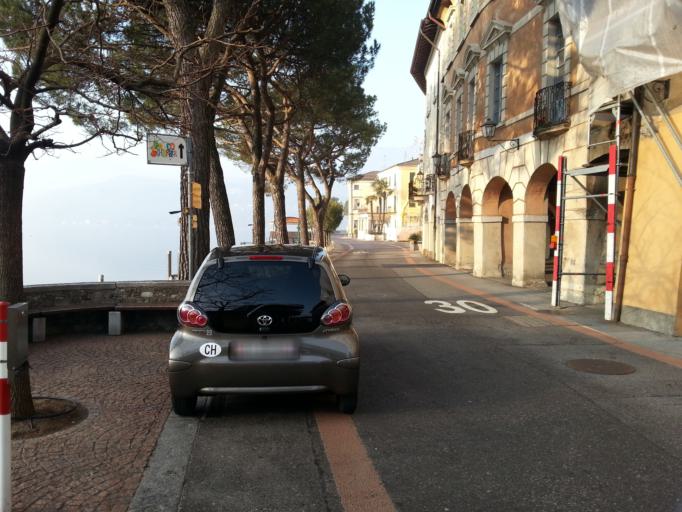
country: IT
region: Lombardy
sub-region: Provincia di Varese
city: Porto Ceresio
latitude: 45.9228
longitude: 8.9170
